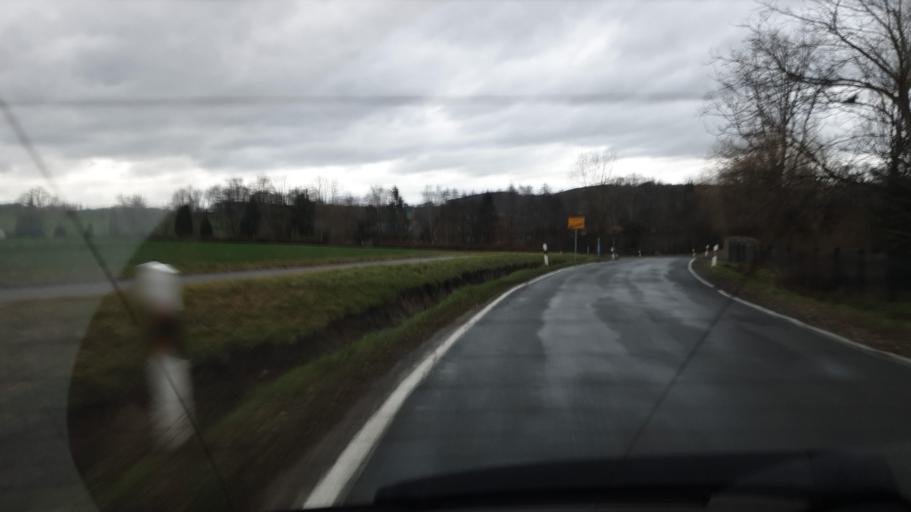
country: DE
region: North Rhine-Westphalia
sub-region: Regierungsbezirk Detmold
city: Lemgo
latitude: 52.0763
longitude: 8.8614
